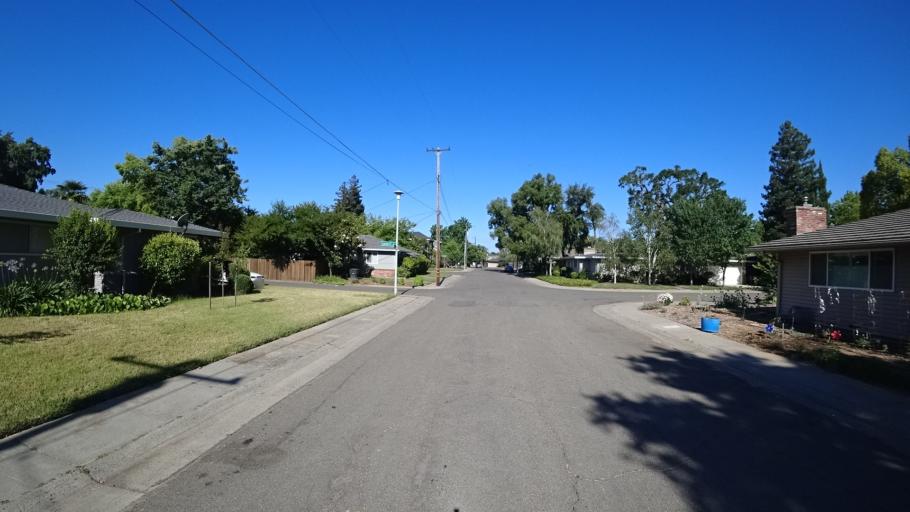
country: US
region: California
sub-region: Sacramento County
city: Parkway
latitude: 38.5255
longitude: -121.5063
